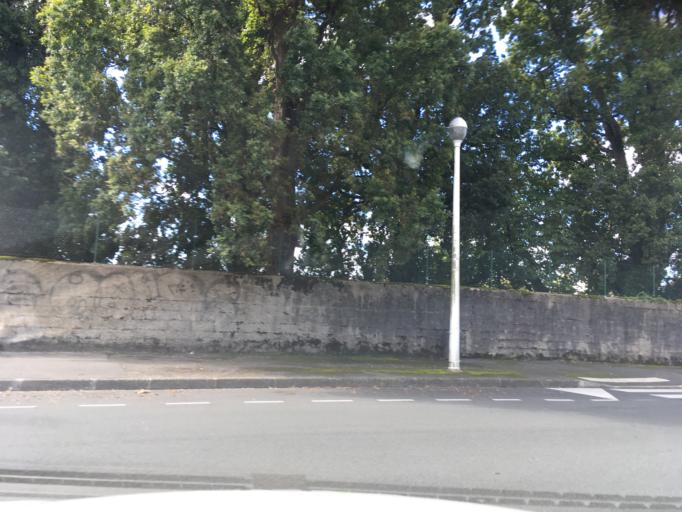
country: FR
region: Aquitaine
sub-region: Departement des Pyrenees-Atlantiques
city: Boucau
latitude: 43.5044
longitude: -1.4667
